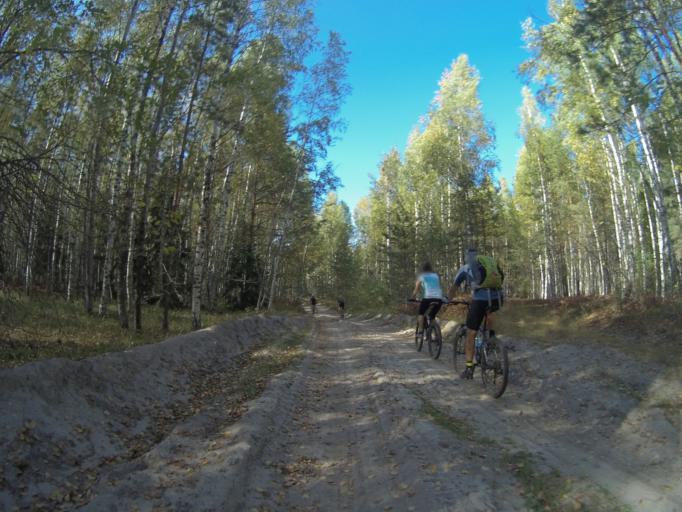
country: RU
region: Vladimir
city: Vorsha
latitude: 55.9011
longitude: 40.1756
